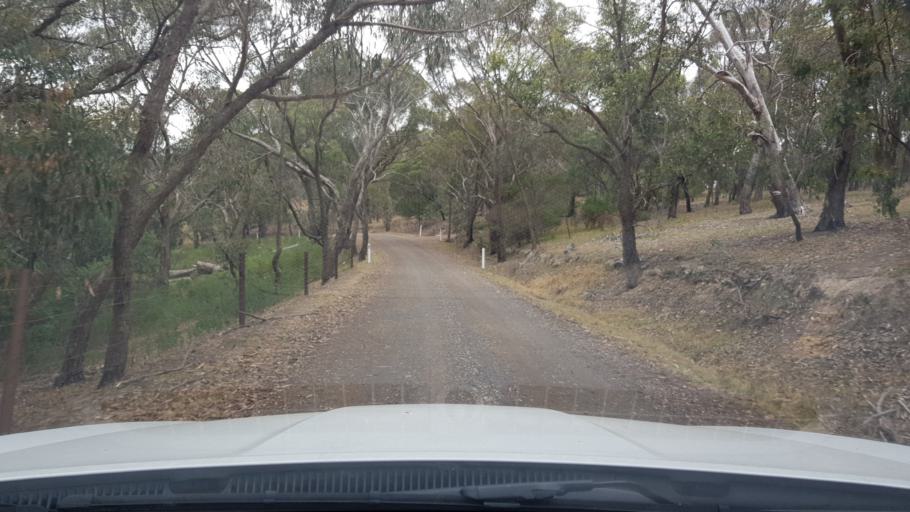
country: AU
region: Victoria
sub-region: Whittlesea
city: Whittlesea
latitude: -37.4849
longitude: 145.0497
